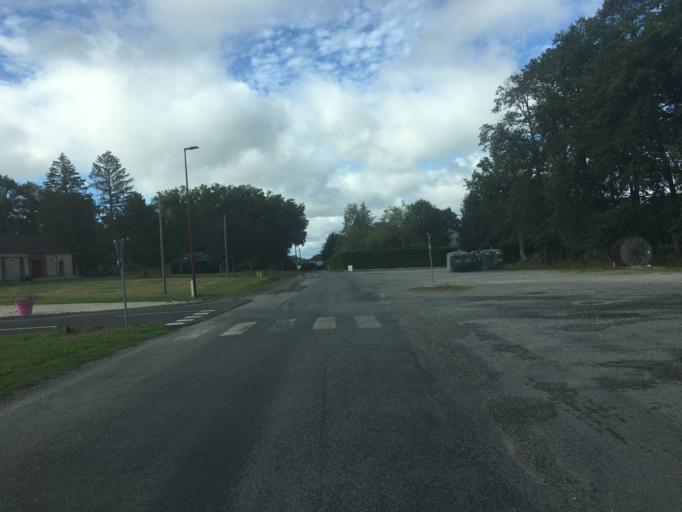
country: FR
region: Limousin
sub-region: Departement de la Correze
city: Bort-les-Orgues
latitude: 45.4159
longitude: 2.4387
